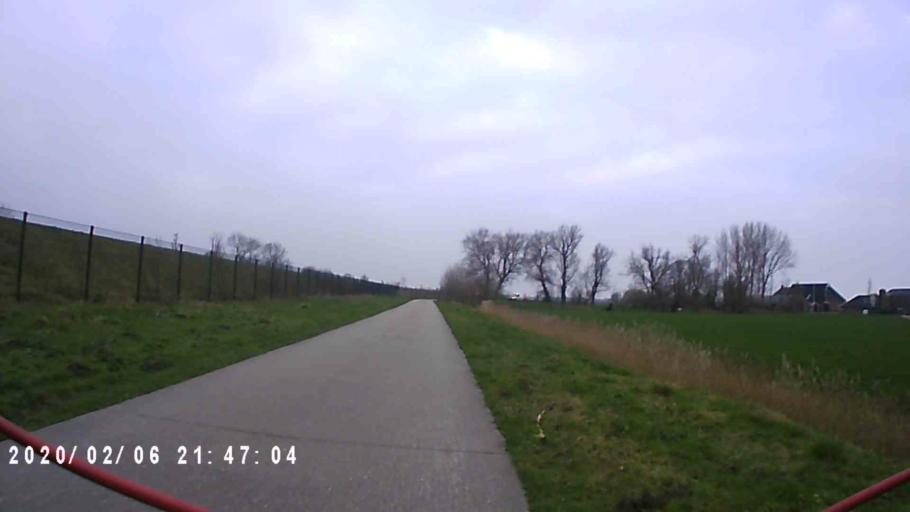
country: NL
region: Groningen
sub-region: Gemeente Zuidhorn
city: Noordhorn
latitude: 53.2553
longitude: 6.3806
